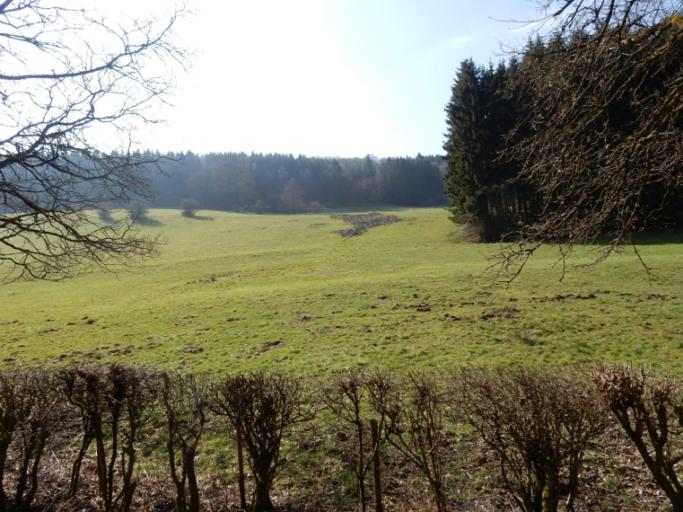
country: LU
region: Diekirch
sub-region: Canton de Wiltz
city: Winseler
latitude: 49.9819
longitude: 5.8601
